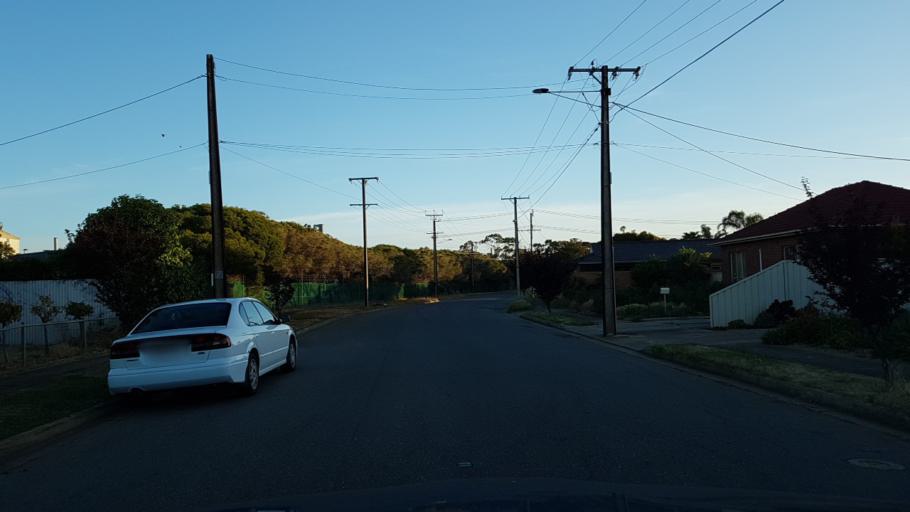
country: AU
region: South Australia
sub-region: Charles Sturt
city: Woodville North
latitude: -34.8637
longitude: 138.5343
